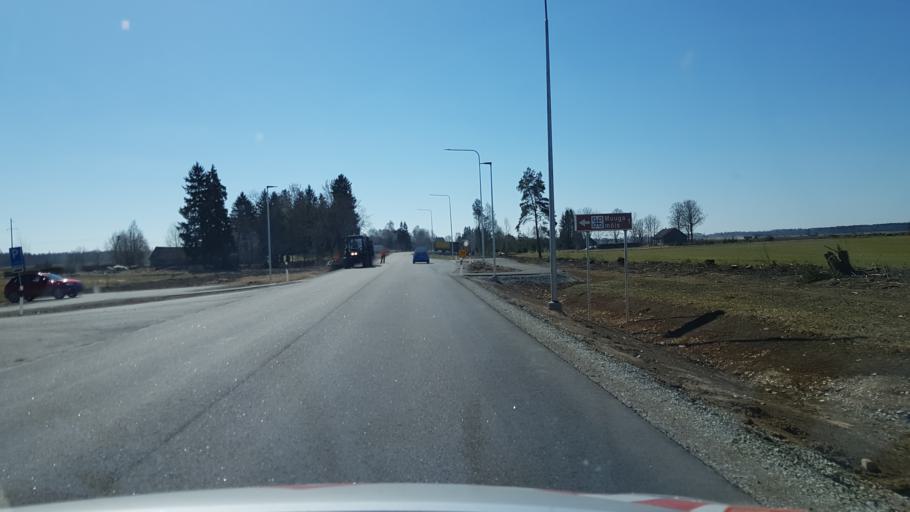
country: EE
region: Laeaene-Virumaa
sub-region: Vinni vald
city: Vinni
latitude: 59.1114
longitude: 26.6180
